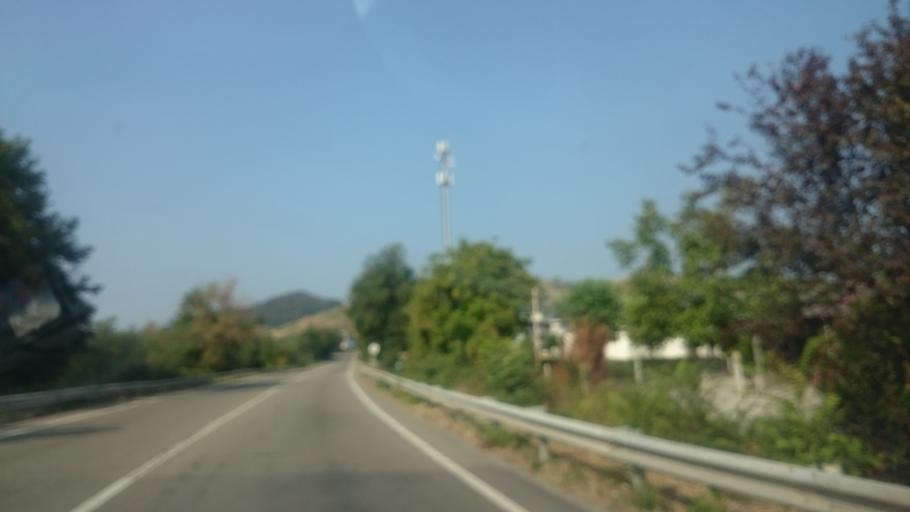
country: IT
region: Emilia-Romagna
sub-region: Provincia di Reggio Emilia
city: Castellarano
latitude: 44.5068
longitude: 10.7332
